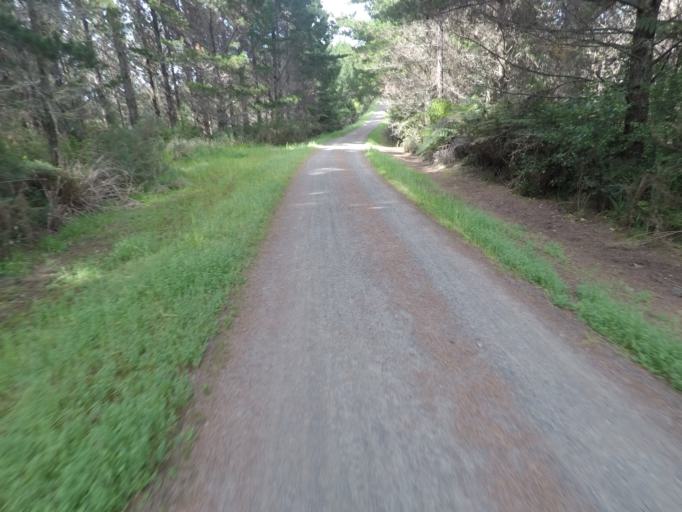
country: NZ
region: Auckland
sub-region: Auckland
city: Muriwai Beach
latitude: -36.7457
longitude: 174.5650
